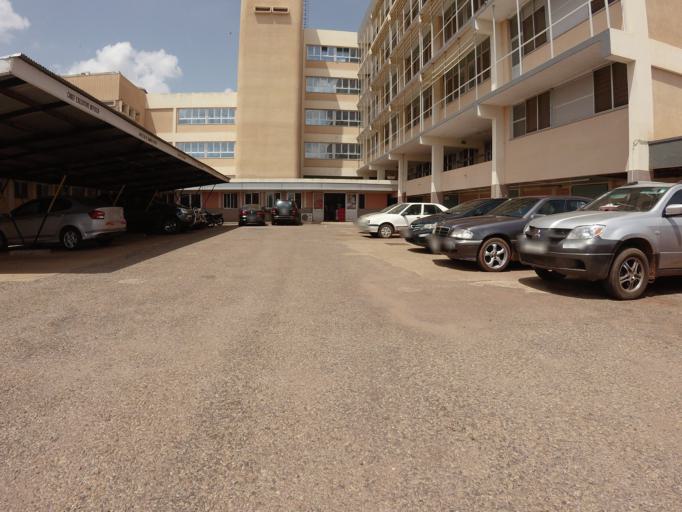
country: GH
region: Northern
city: Tamale
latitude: 9.3928
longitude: -0.8239
